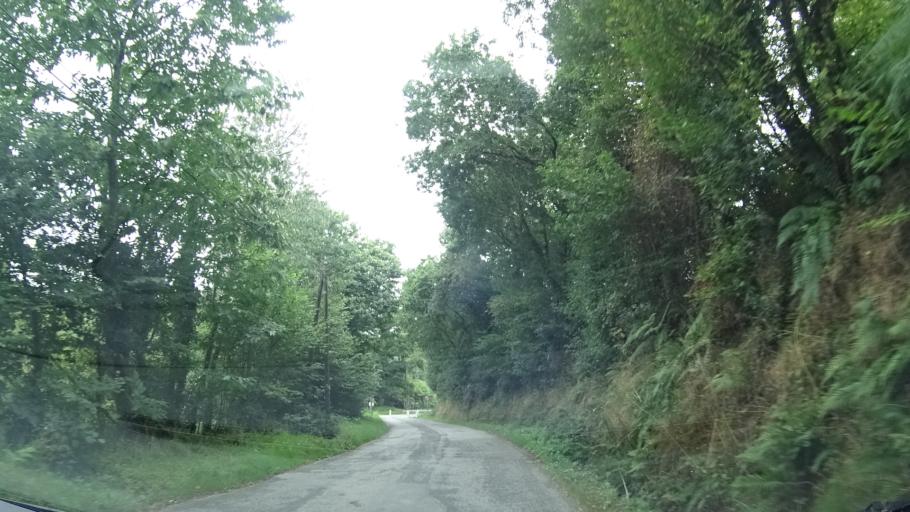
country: FR
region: Brittany
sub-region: Departement du Finistere
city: Chateaulin
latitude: 48.1964
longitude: -4.1045
